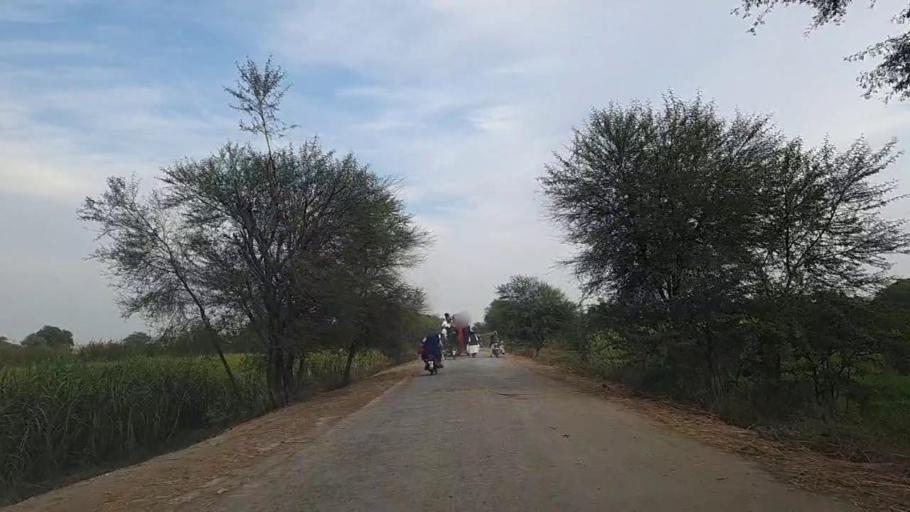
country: PK
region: Sindh
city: Daur
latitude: 26.5269
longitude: 68.4105
